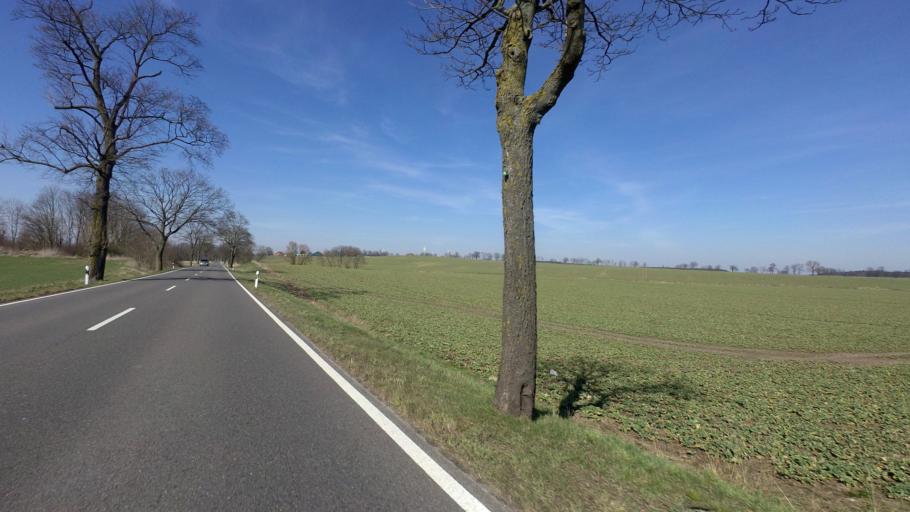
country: DE
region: Brandenburg
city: Protzel
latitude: 52.6211
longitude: 14.0177
